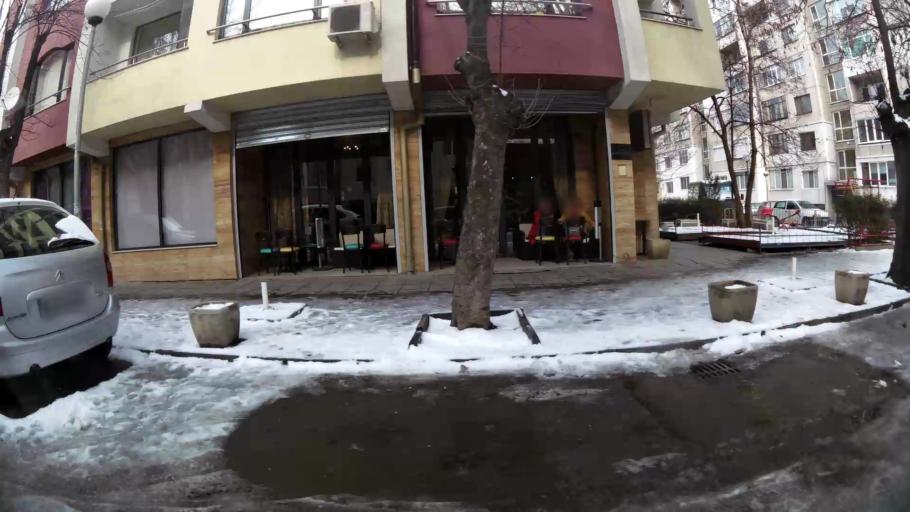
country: BG
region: Sofia-Capital
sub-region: Stolichna Obshtina
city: Sofia
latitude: 42.7047
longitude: 23.3490
